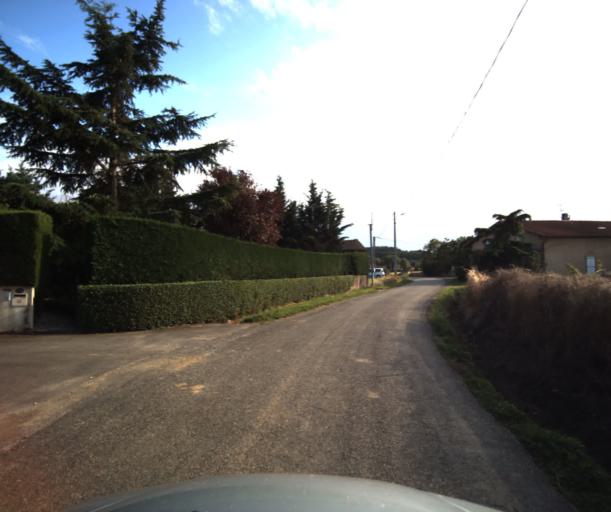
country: FR
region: Midi-Pyrenees
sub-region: Departement de la Haute-Garonne
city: Eaunes
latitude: 43.4418
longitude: 1.3376
